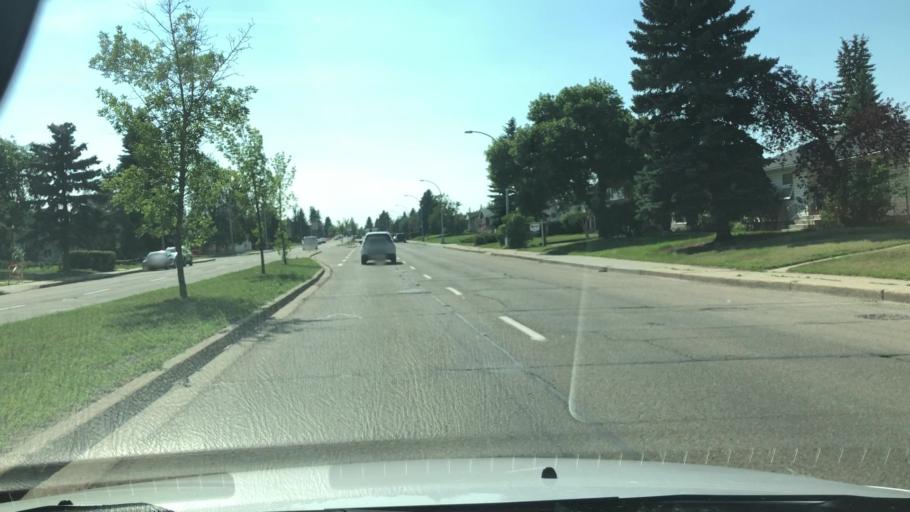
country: CA
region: Alberta
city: Edmonton
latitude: 53.6070
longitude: -113.4617
